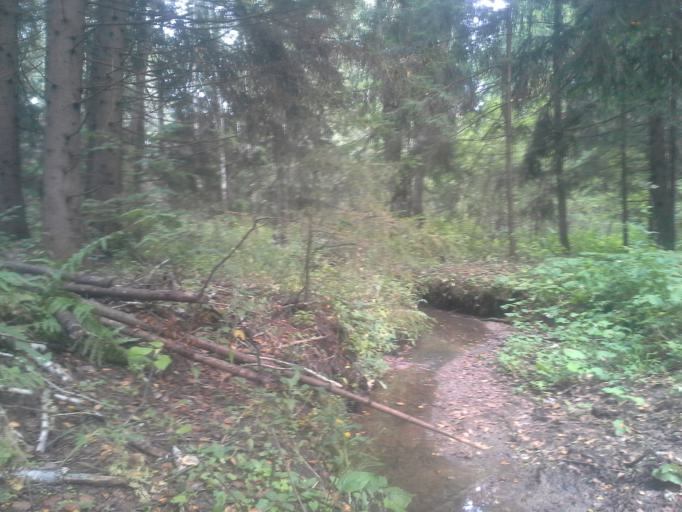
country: RU
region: Moskovskaya
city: Kievskij
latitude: 55.3514
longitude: 36.9652
